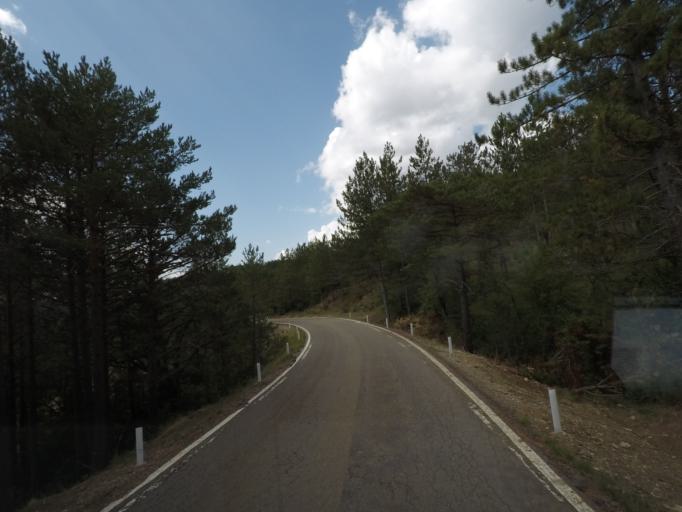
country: ES
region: Aragon
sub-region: Provincia de Huesca
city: Fiscal
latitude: 42.4077
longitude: -0.1613
